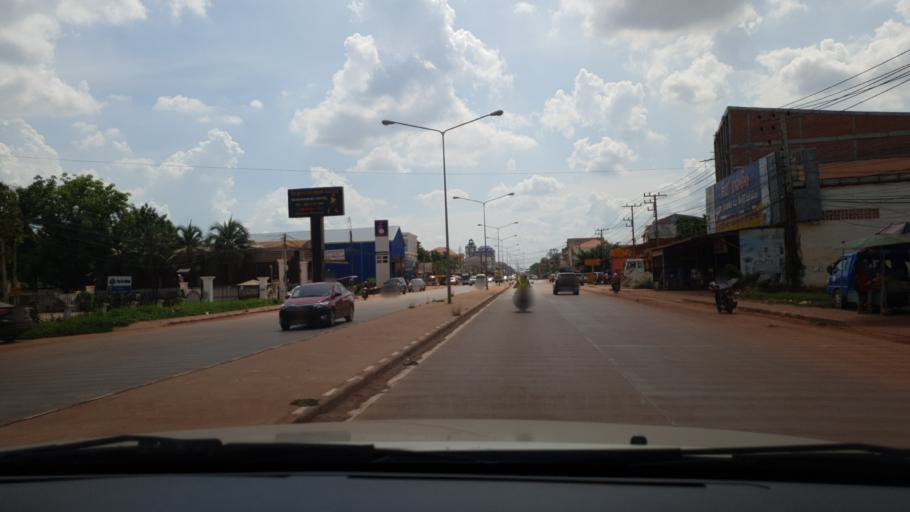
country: LA
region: Vientiane
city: Vientiane
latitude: 18.0316
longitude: 102.6481
